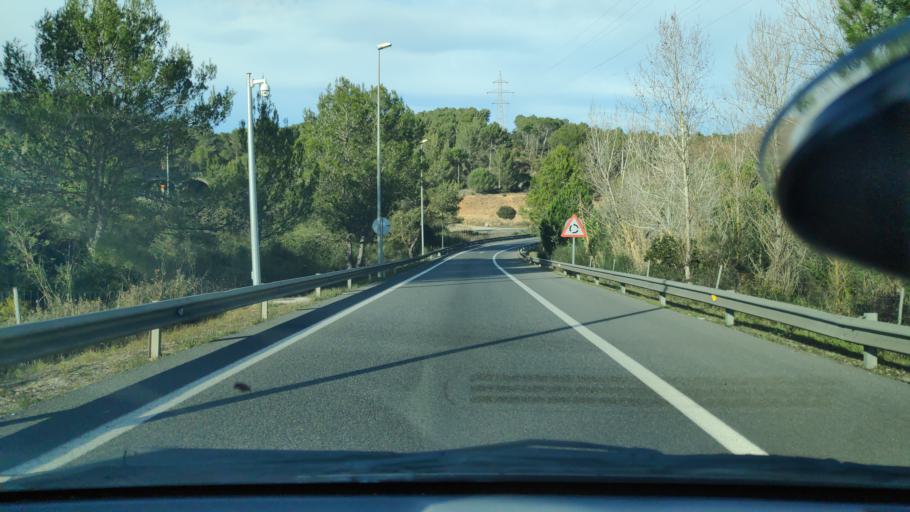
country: ES
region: Catalonia
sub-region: Provincia de Barcelona
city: Rubi
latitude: 41.5095
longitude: 2.0490
